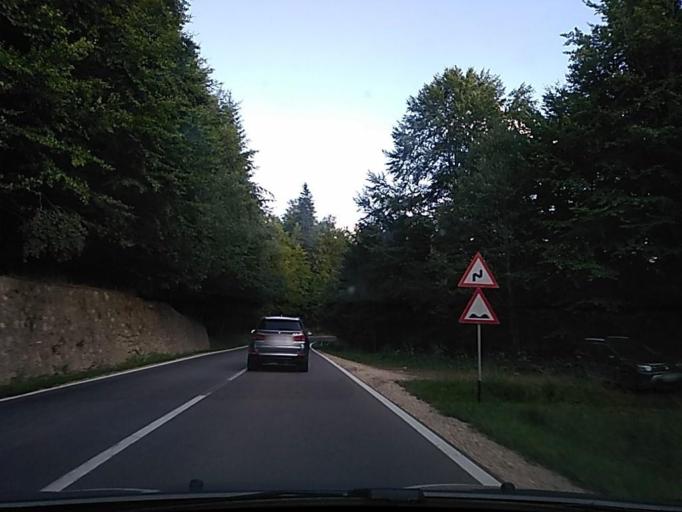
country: RO
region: Brasov
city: Crivina
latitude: 45.4671
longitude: 25.9390
